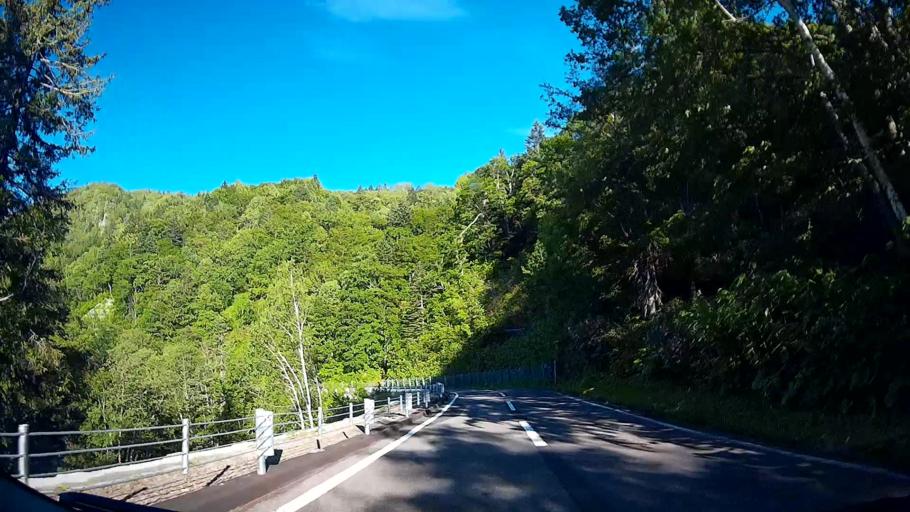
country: JP
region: Hokkaido
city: Otaru
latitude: 42.9868
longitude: 141.0734
